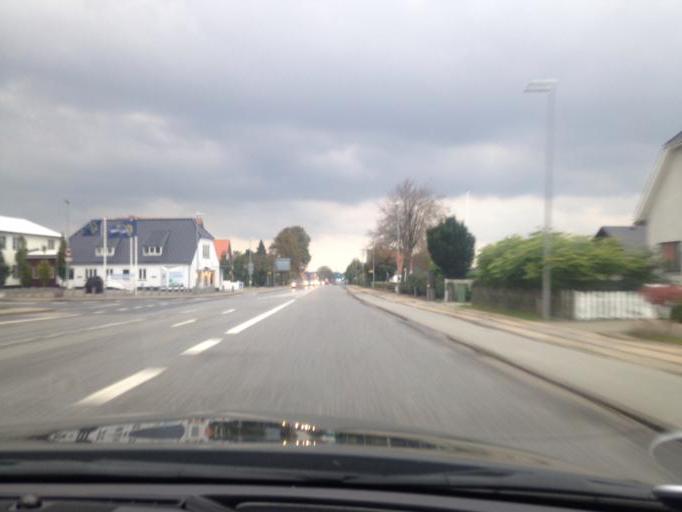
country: DK
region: South Denmark
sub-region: Kolding Kommune
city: Kolding
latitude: 55.4715
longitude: 9.4707
